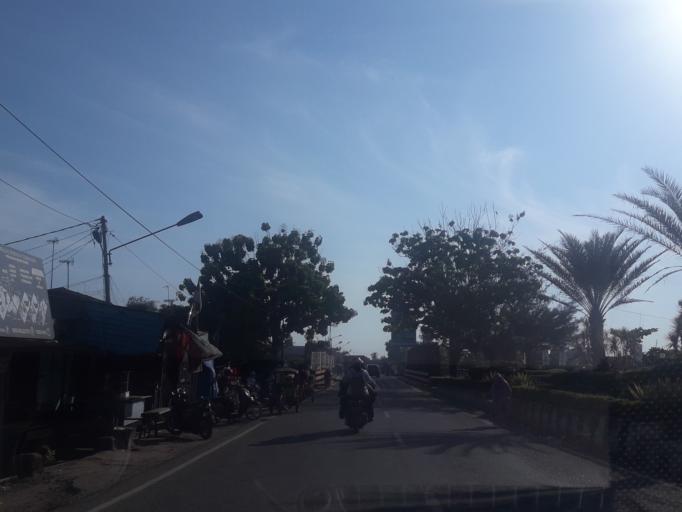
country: ID
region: South Kalimantan
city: Martapura
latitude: -3.4024
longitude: 114.8478
